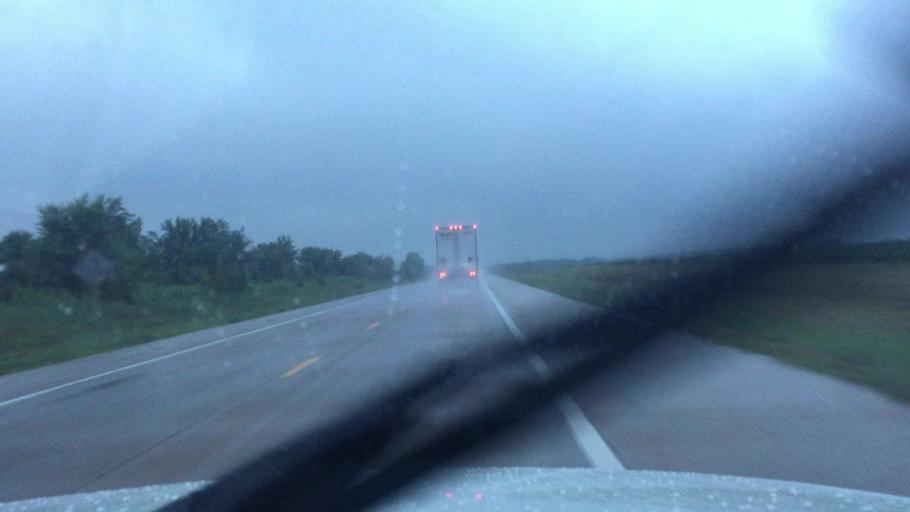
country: US
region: Kansas
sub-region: Neosho County
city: Chanute
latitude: 37.5709
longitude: -95.4709
